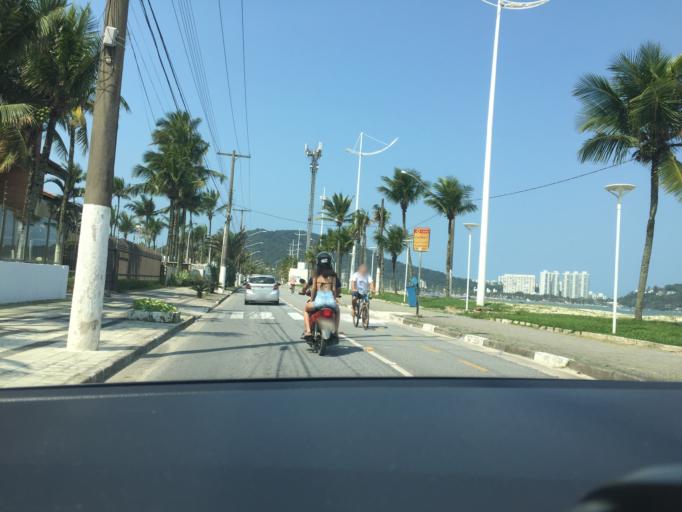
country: BR
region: Sao Paulo
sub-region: Guaruja
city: Guaruja
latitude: -23.9848
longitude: -46.2164
